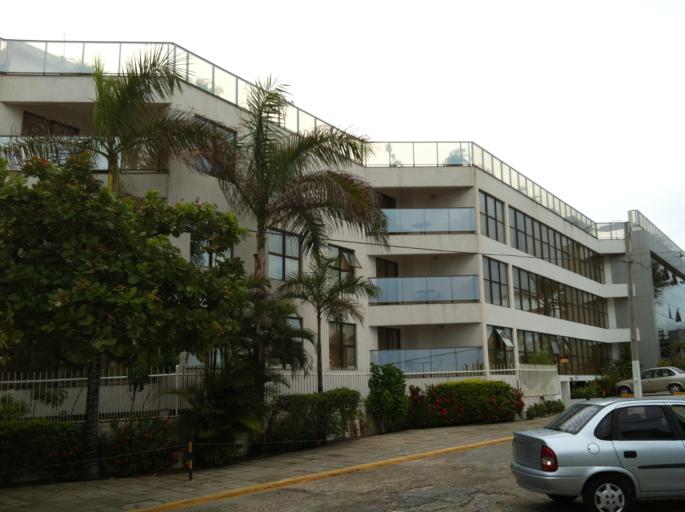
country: BR
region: Rio Grande do Norte
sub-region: Natal
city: Natal
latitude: -5.8726
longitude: -35.1780
